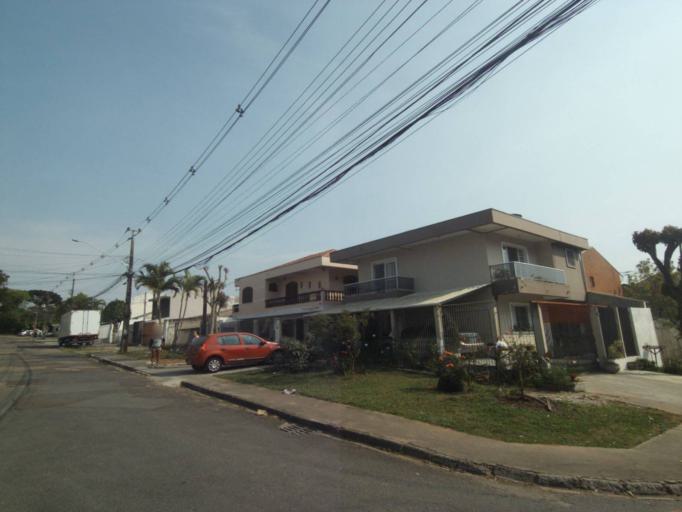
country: BR
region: Parana
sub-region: Pinhais
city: Pinhais
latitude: -25.4816
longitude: -49.2035
